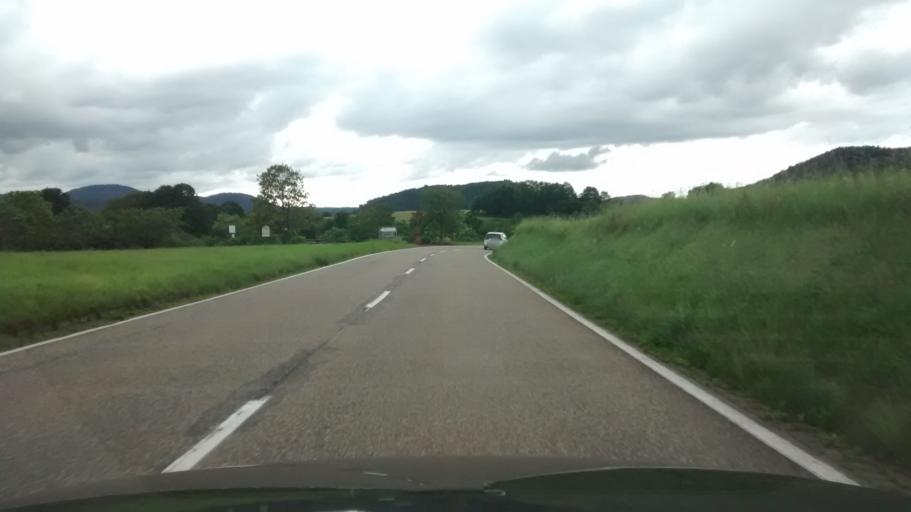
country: DE
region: Rheinland-Pfalz
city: Busenberg
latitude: 49.1256
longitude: 7.8391
